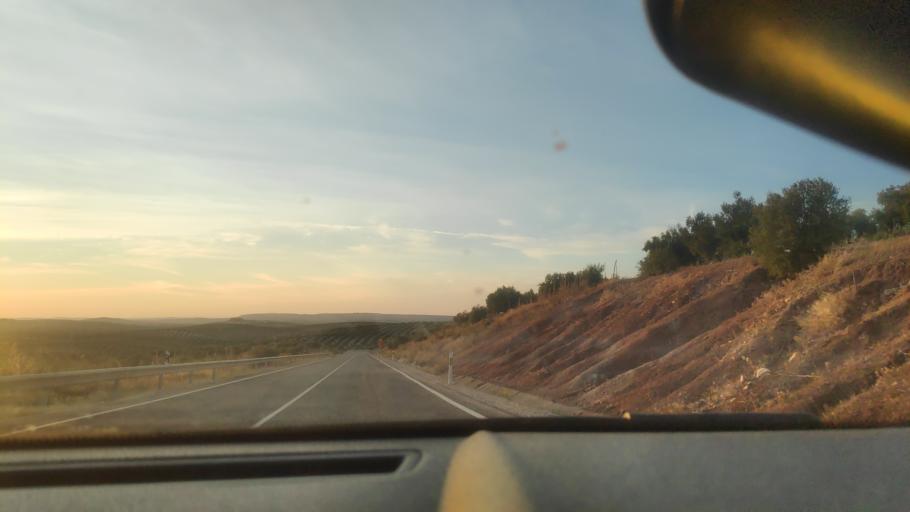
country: ES
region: Andalusia
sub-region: Provincia de Jaen
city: Villardompardo
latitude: 37.8262
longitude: -4.0446
